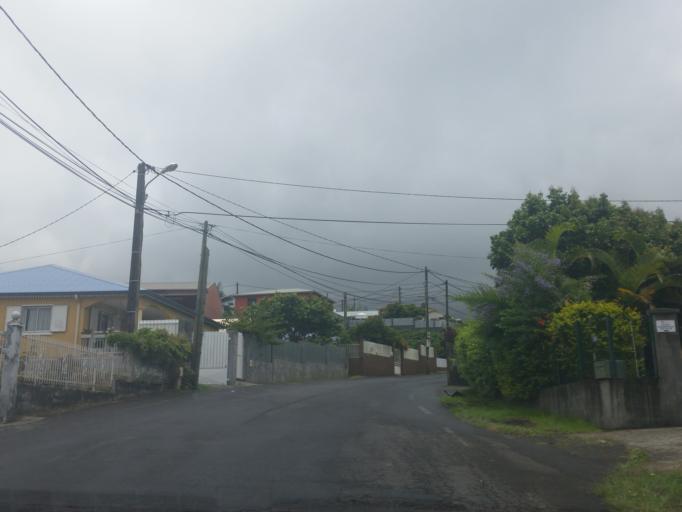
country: RE
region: Reunion
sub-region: Reunion
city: Le Tampon
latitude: -21.2429
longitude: 55.5132
